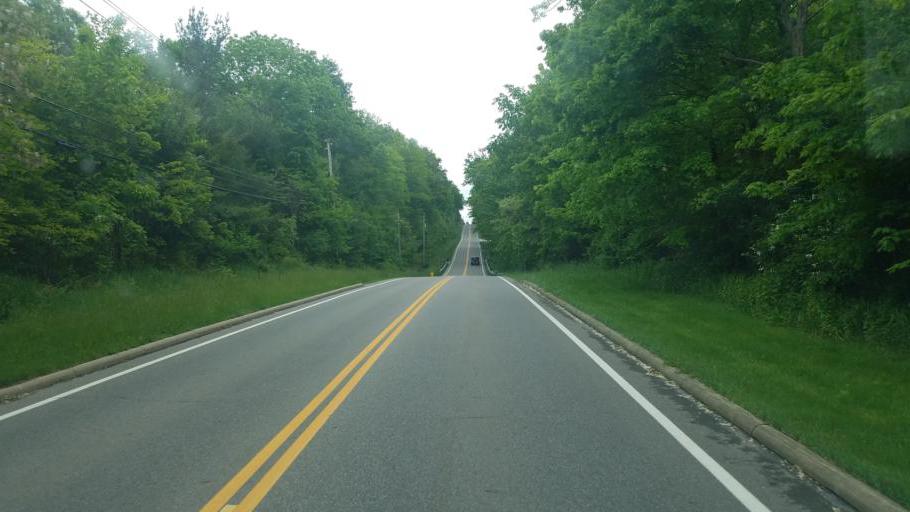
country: US
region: Ohio
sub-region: Geauga County
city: Bainbridge
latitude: 41.3620
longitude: -81.3574
